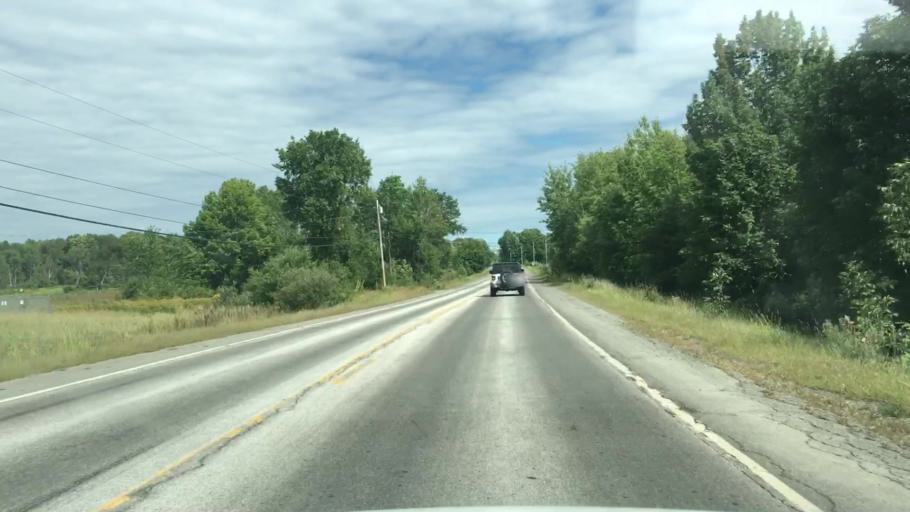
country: US
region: Maine
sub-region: Piscataquis County
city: Dover-Foxcroft
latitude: 45.1550
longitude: -69.2353
